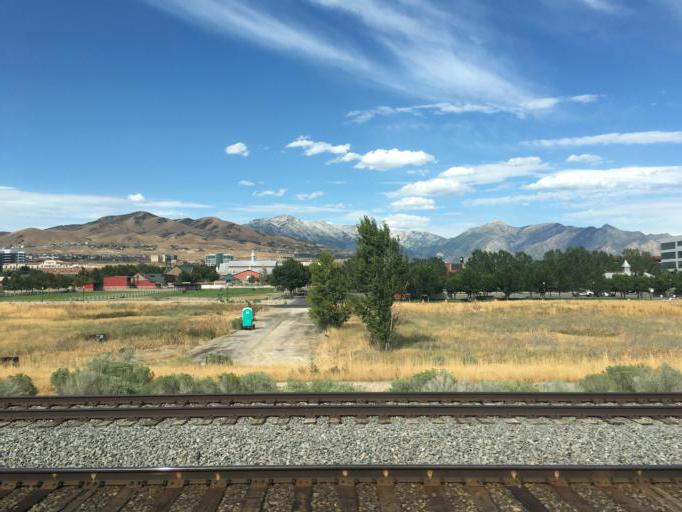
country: US
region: Utah
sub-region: Utah County
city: Lehi
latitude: 40.4210
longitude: -111.8916
